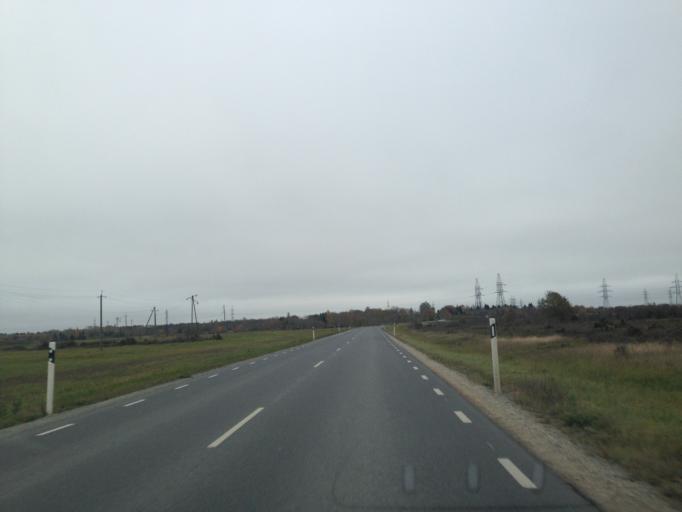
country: EE
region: Harju
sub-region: Harku vald
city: Tabasalu
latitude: 59.3963
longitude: 24.5532
